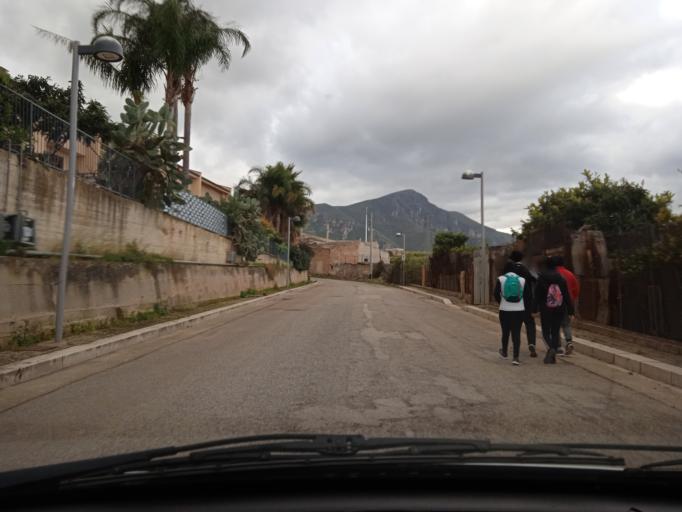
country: IT
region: Sicily
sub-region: Palermo
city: Villabate
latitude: 38.0732
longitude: 13.4393
